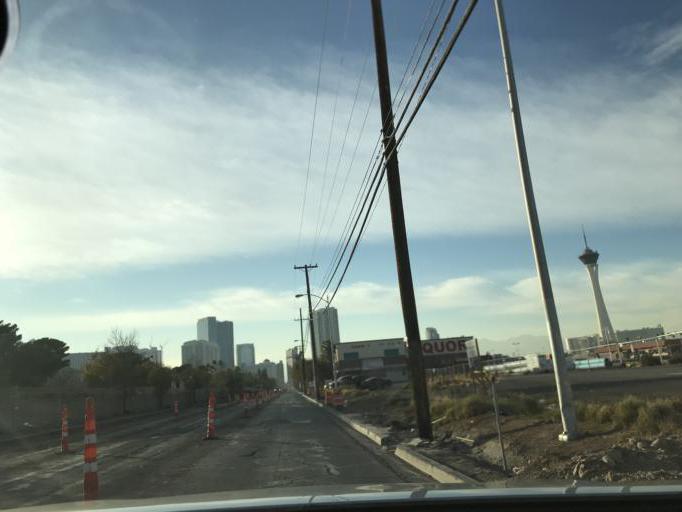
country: US
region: Nevada
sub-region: Clark County
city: Winchester
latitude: 36.1406
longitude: -115.1401
